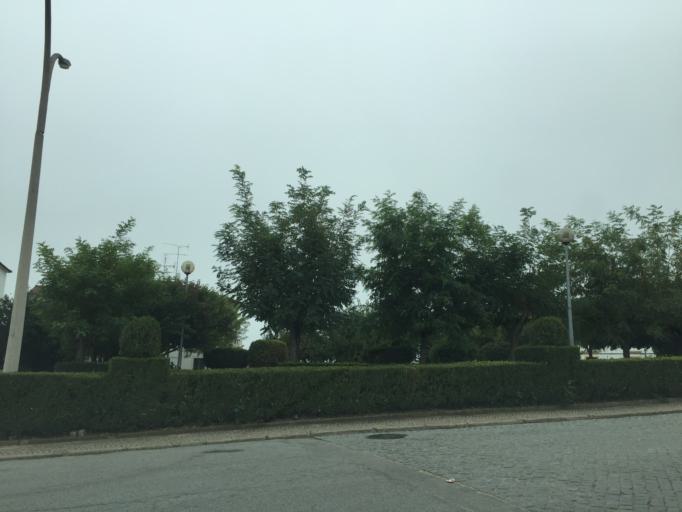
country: PT
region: Portalegre
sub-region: Arronches
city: Arronches
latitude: 39.0540
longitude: -7.4372
